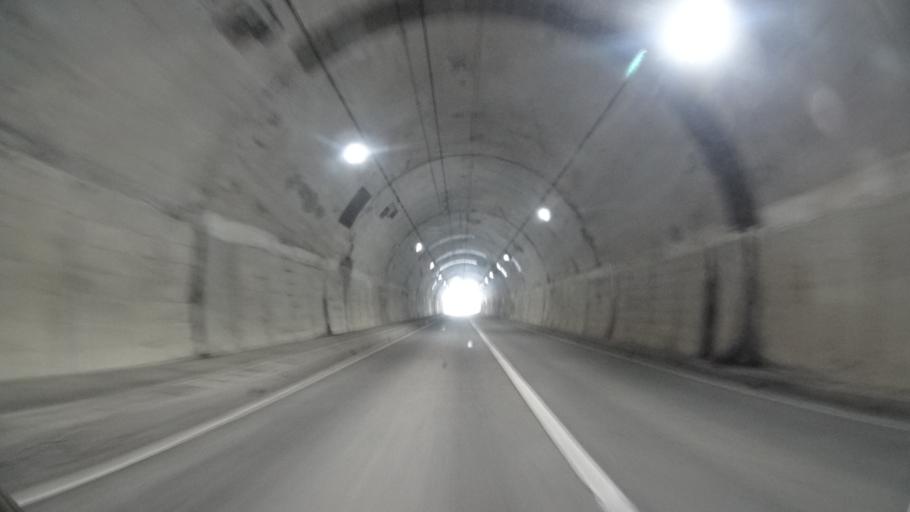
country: JP
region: Ehime
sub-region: Nishiuwa-gun
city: Ikata-cho
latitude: 33.3955
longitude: 132.1398
